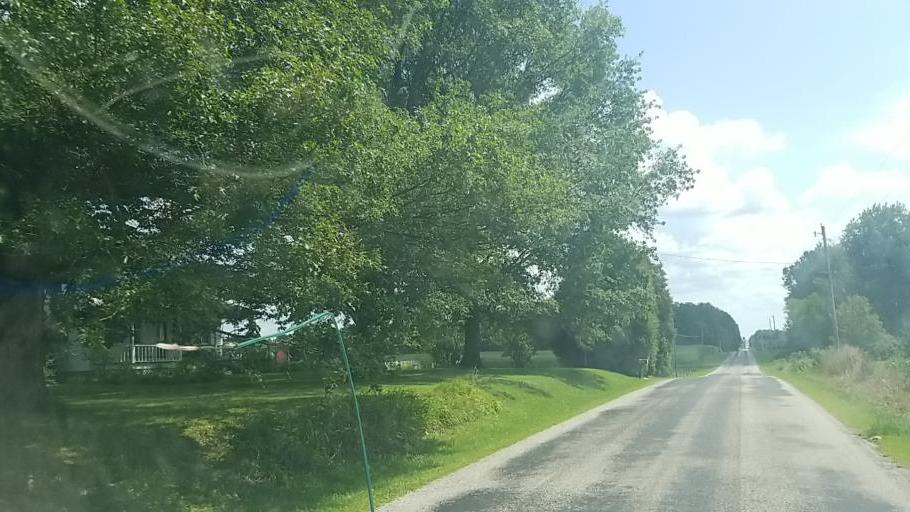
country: US
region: Ohio
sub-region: Wayne County
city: West Salem
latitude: 40.9742
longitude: -82.0822
